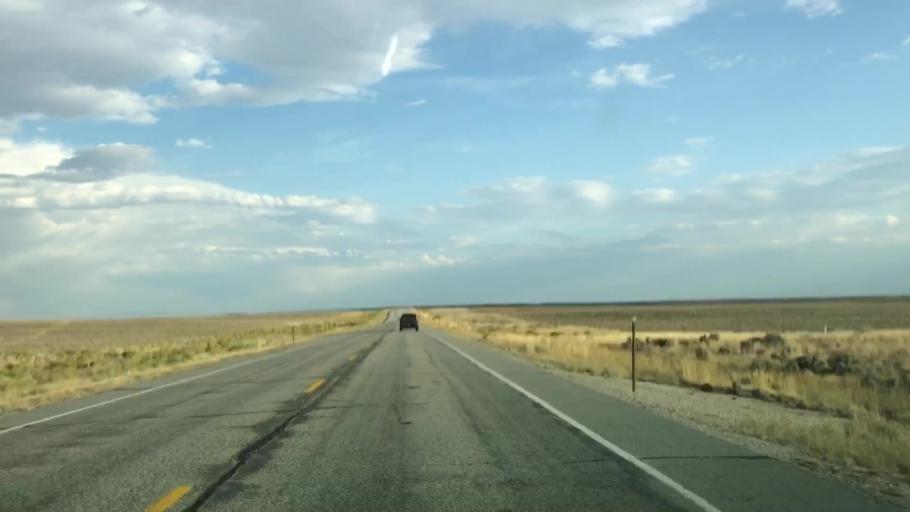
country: US
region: Wyoming
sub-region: Sublette County
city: Marbleton
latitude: 42.3250
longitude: -109.5118
